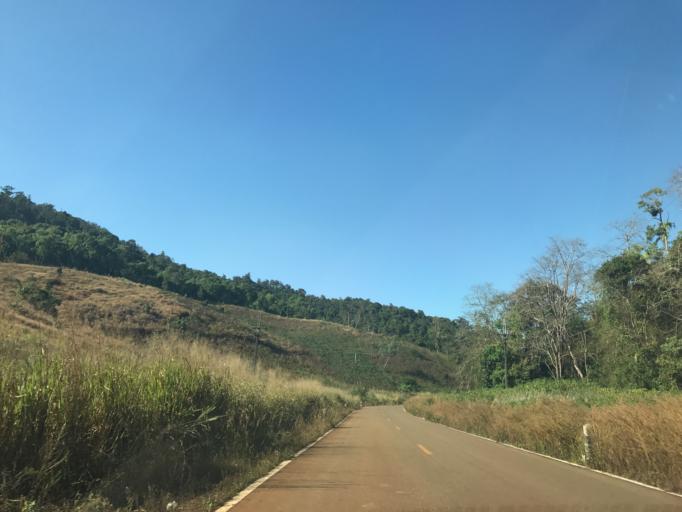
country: TH
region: Tak
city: Phop Phra
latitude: 16.5543
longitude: 98.8113
